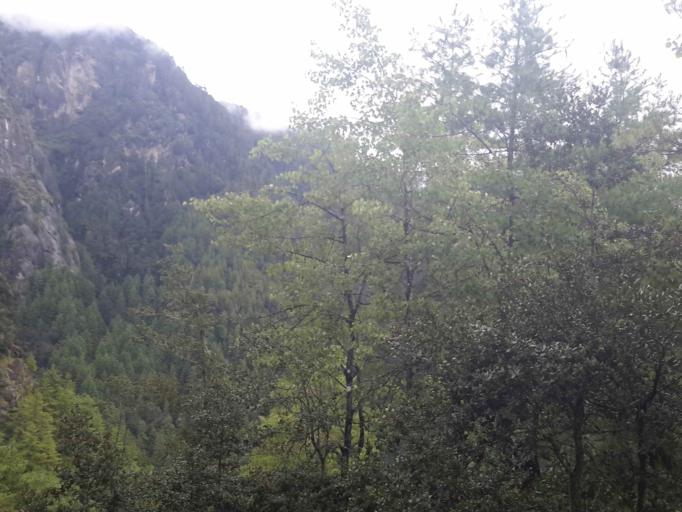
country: BT
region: Paro
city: Paro
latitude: 27.4870
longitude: 89.3576
